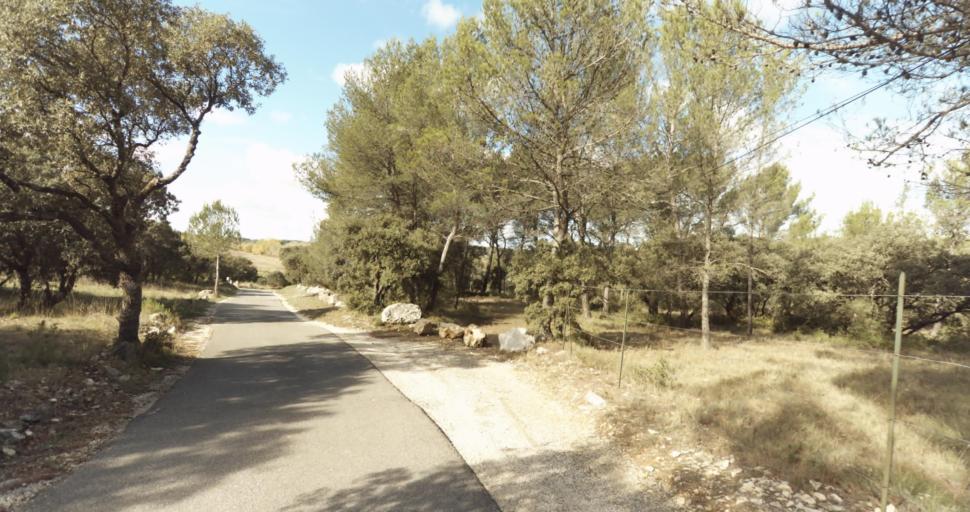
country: FR
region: Provence-Alpes-Cote d'Azur
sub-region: Departement des Bouches-du-Rhone
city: Venelles
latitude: 43.5852
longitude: 5.5012
